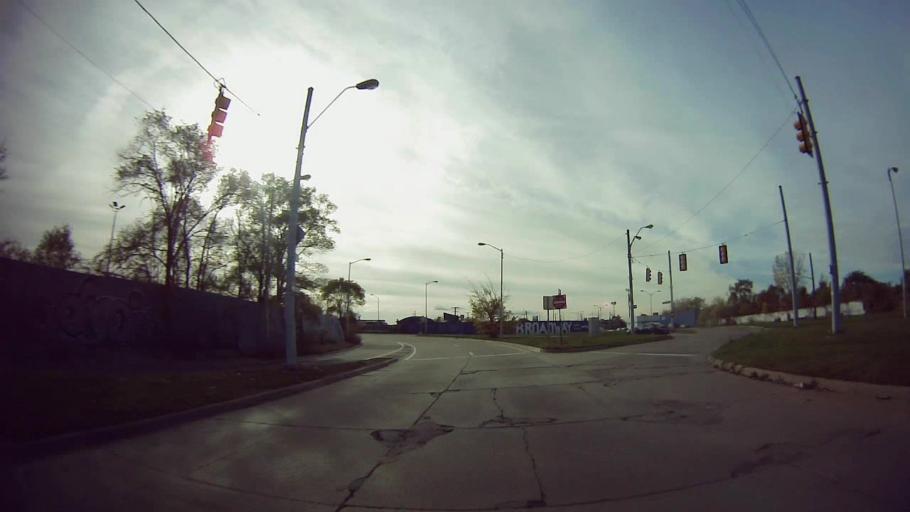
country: US
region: Michigan
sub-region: Wayne County
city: Hamtramck
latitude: 42.4080
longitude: -83.0425
